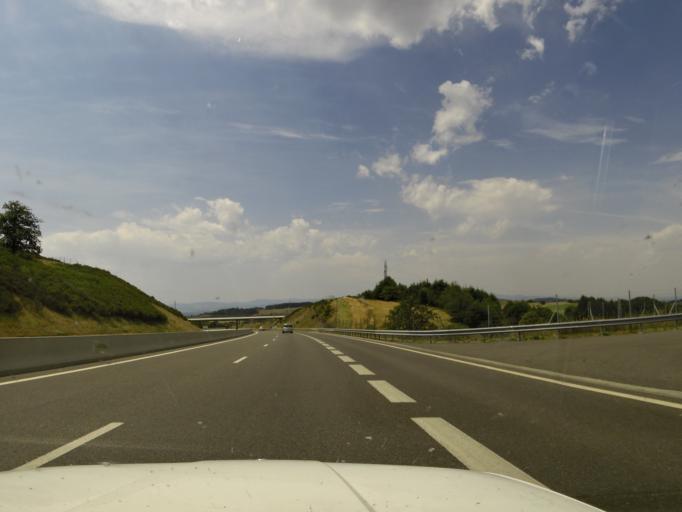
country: FR
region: Rhone-Alpes
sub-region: Departement de la Loire
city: Bussieres
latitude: 45.8711
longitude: 4.2935
